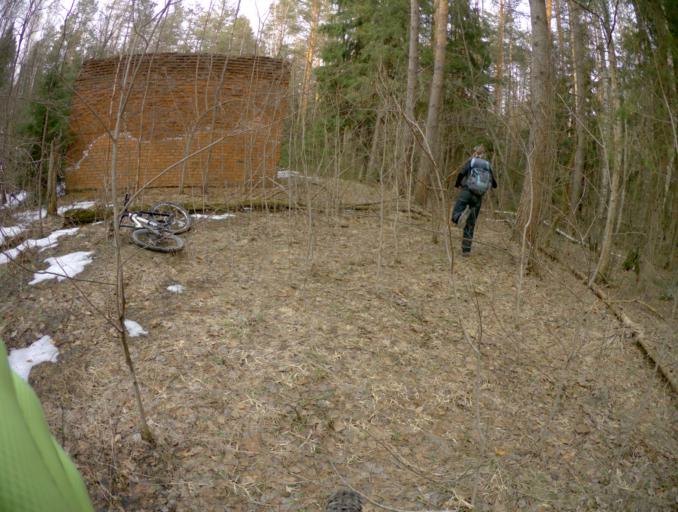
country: RU
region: Vladimir
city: Kommunar
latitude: 56.0753
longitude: 40.4455
